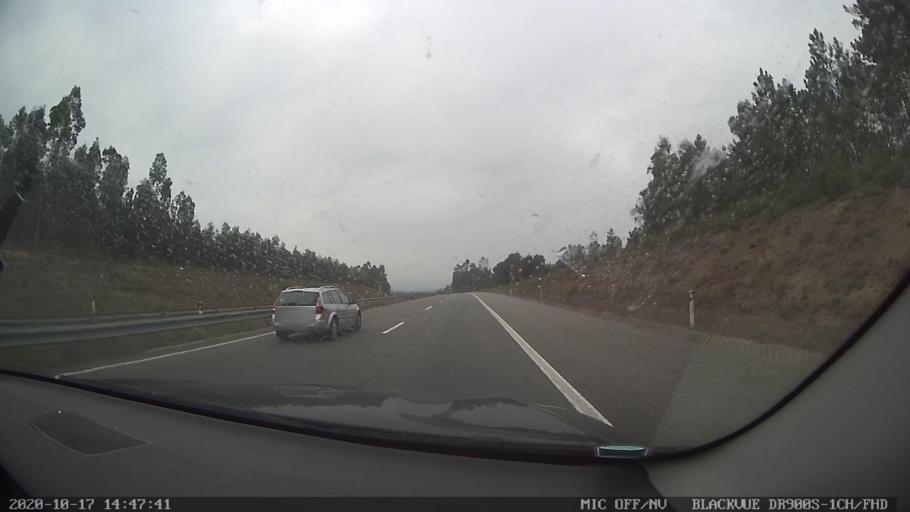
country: PT
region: Braga
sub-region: Barcelos
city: Galegos
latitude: 41.5382
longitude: -8.5280
